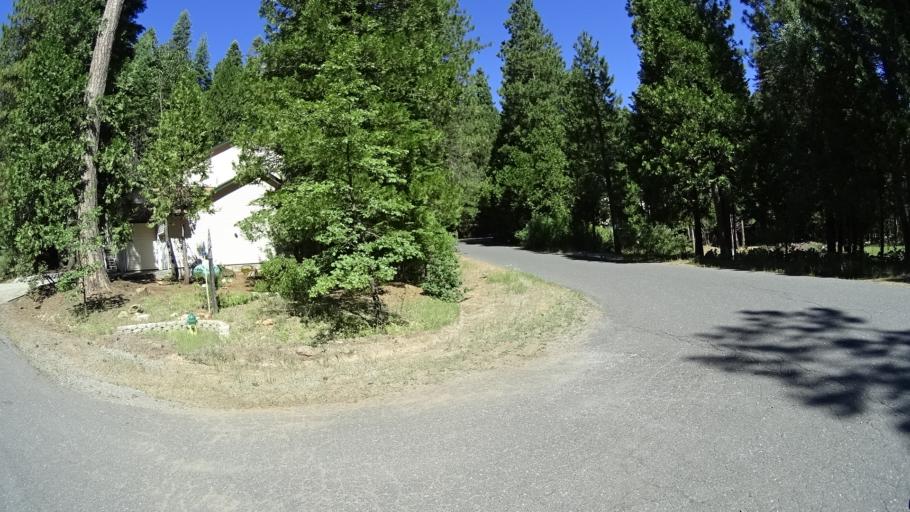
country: US
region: California
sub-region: Calaveras County
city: Arnold
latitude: 38.2919
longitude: -120.2765
